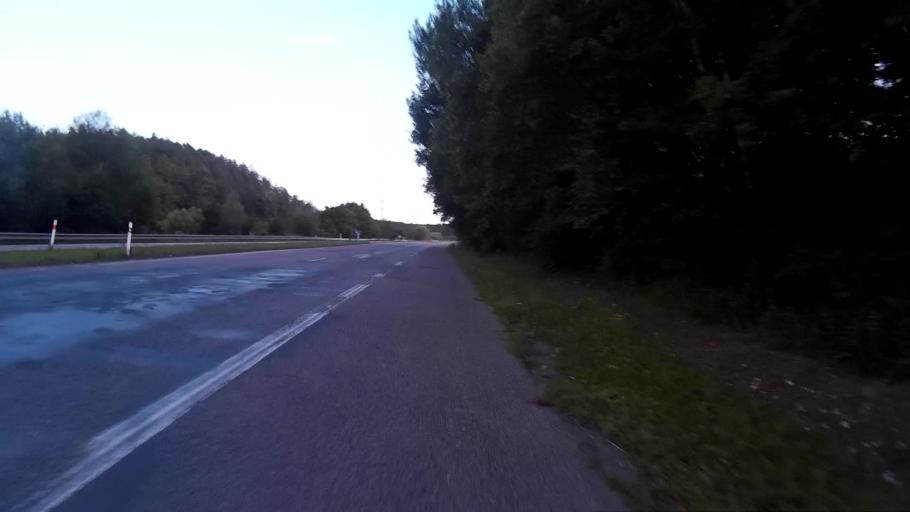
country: CZ
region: South Moravian
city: Troubsko
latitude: 49.2058
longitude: 16.5197
